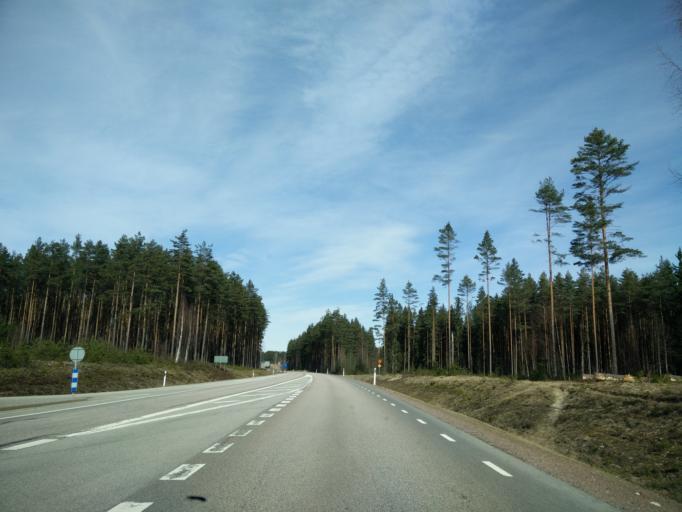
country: SE
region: Vaermland
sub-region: Hagfors Kommun
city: Hagfors
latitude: 60.0269
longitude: 13.5901
